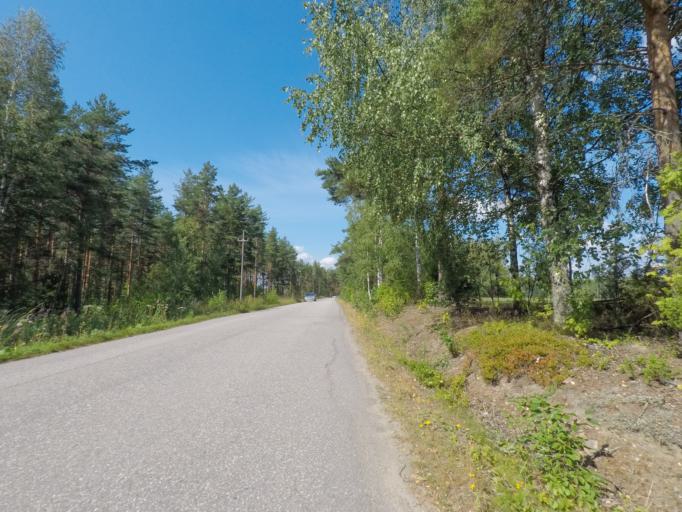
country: FI
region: Southern Savonia
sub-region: Mikkeli
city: Puumala
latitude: 61.4481
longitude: 28.1593
